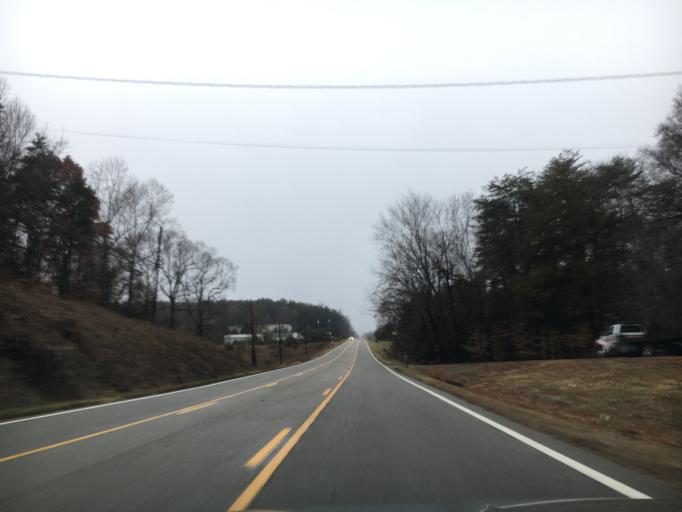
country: US
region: Virginia
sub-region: Prince Edward County
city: Farmville
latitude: 37.3158
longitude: -78.4461
